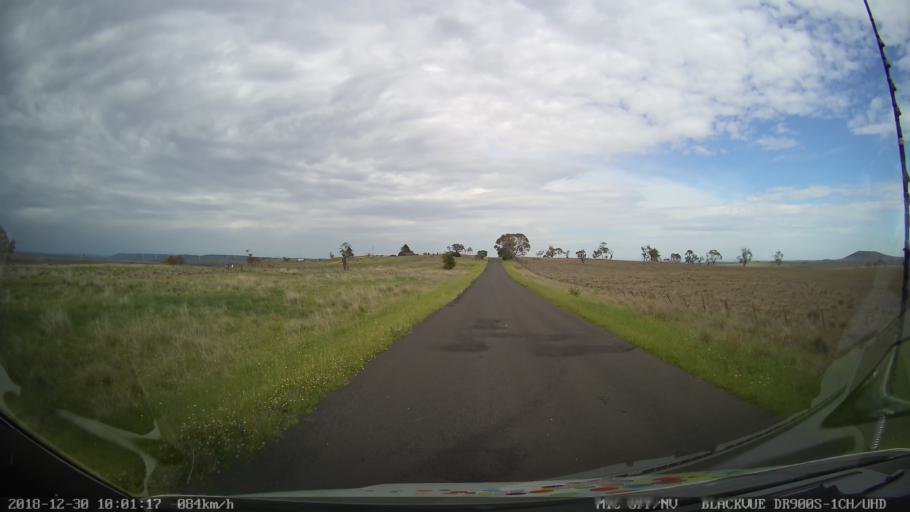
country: AU
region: New South Wales
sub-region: Cooma-Monaro
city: Cooma
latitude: -36.5148
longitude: 149.1883
